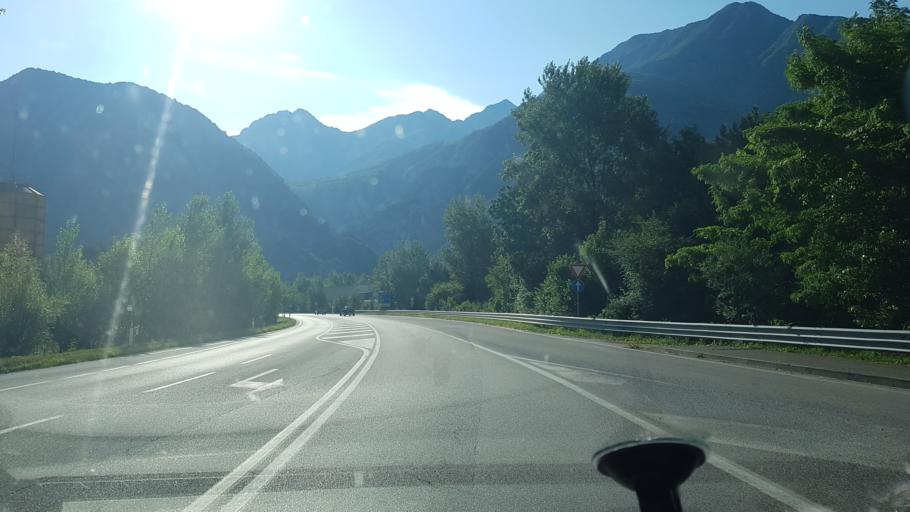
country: IT
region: Friuli Venezia Giulia
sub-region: Provincia di Udine
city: Amaro
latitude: 46.3799
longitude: 13.1273
